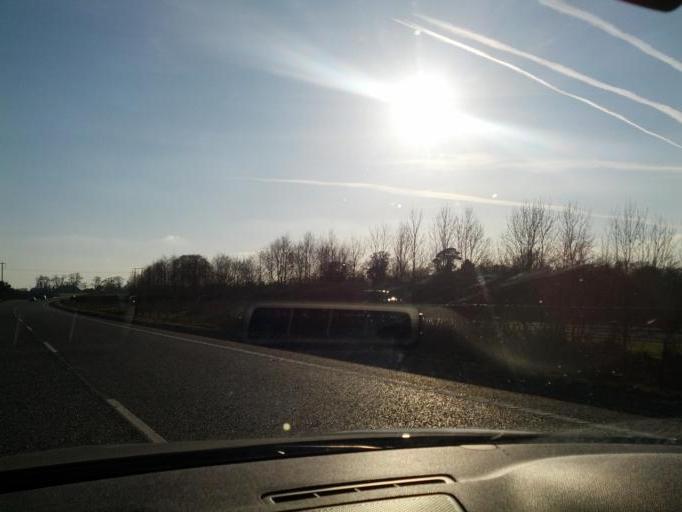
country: IE
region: Leinster
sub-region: Laois
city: Portlaoise
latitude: 53.0213
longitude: -7.2616
